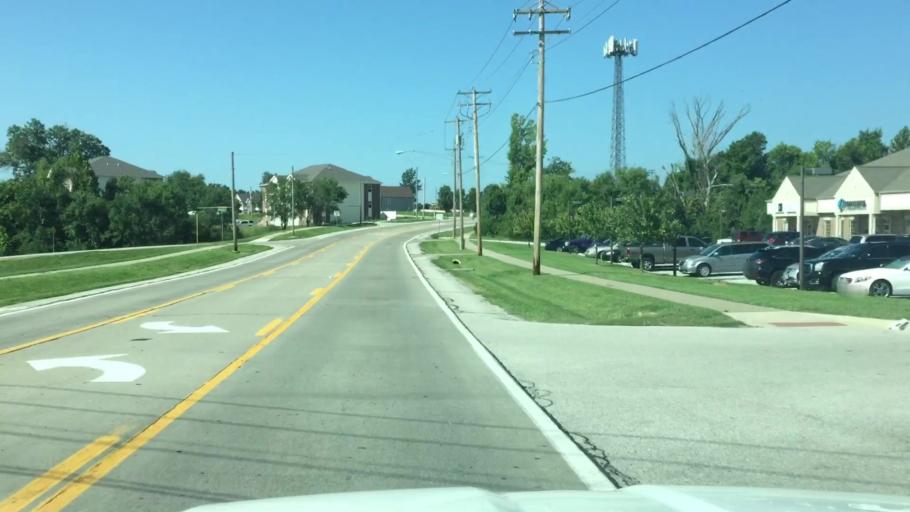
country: US
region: Missouri
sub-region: Jefferson County
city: Arnold
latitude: 38.4624
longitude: -90.3687
